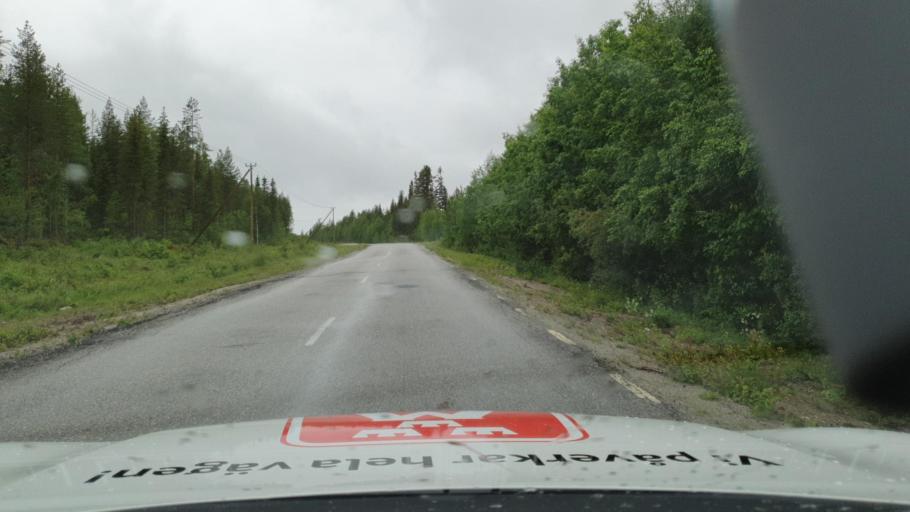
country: SE
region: Vaesterbotten
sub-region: Asele Kommun
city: Asele
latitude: 64.0062
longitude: 17.2084
